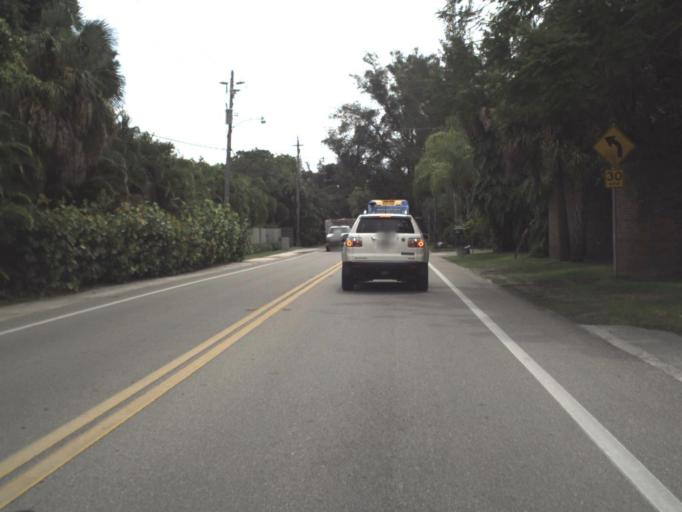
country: US
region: Florida
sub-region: Sarasota County
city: Siesta Key
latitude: 27.2925
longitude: -82.5589
